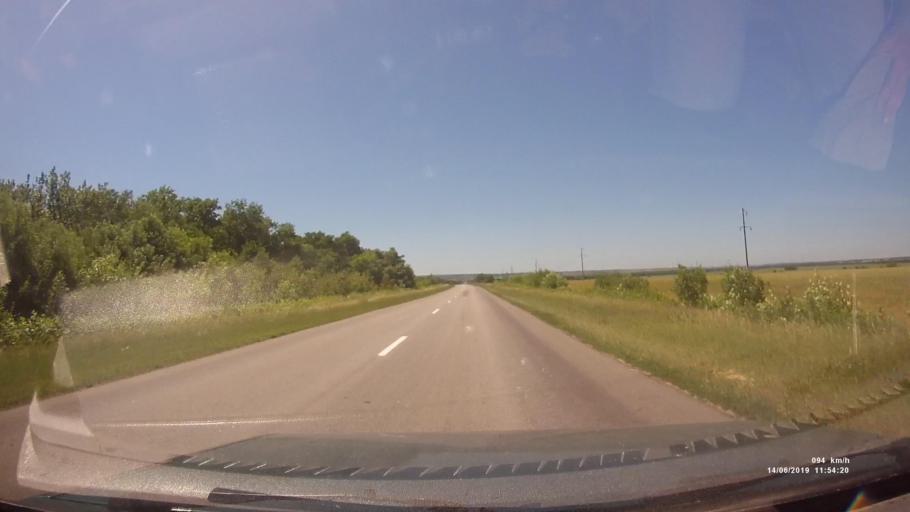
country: RU
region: Rostov
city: Kazanskaya
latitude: 49.8199
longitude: 41.1961
